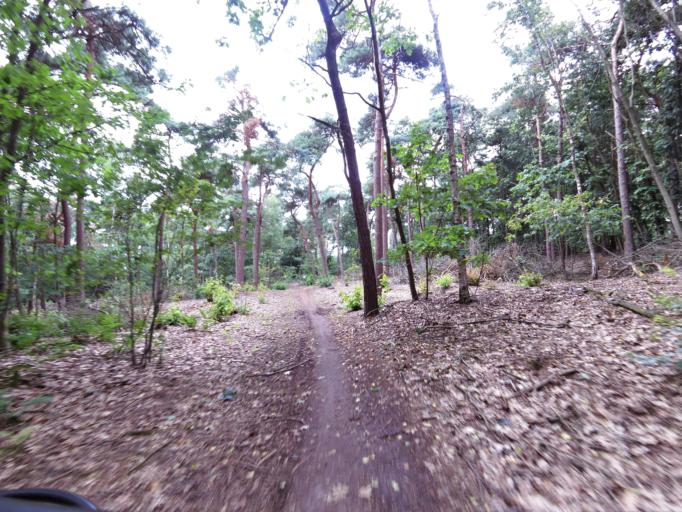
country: NL
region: North Brabant
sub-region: Gemeente Son en Breugel
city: Breugel
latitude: 51.5551
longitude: 5.5037
